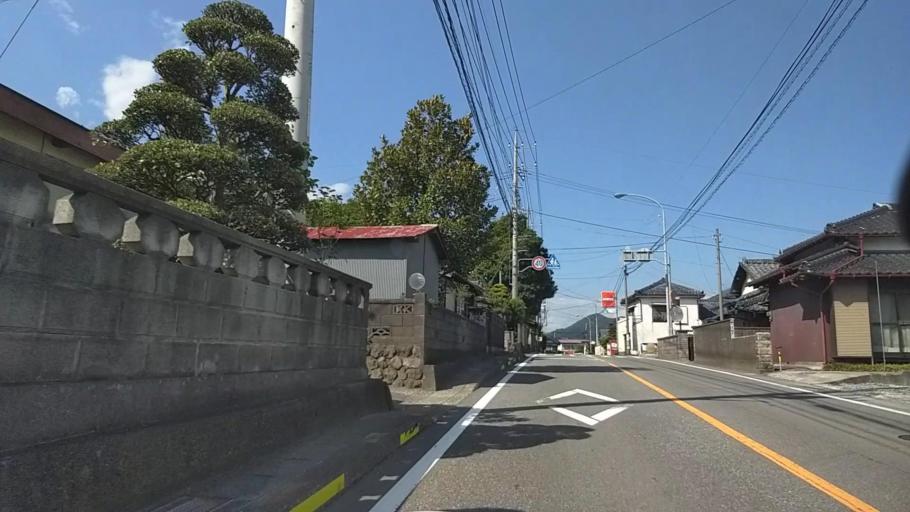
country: JP
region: Yamanashi
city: Ryuo
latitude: 35.4078
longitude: 138.4421
